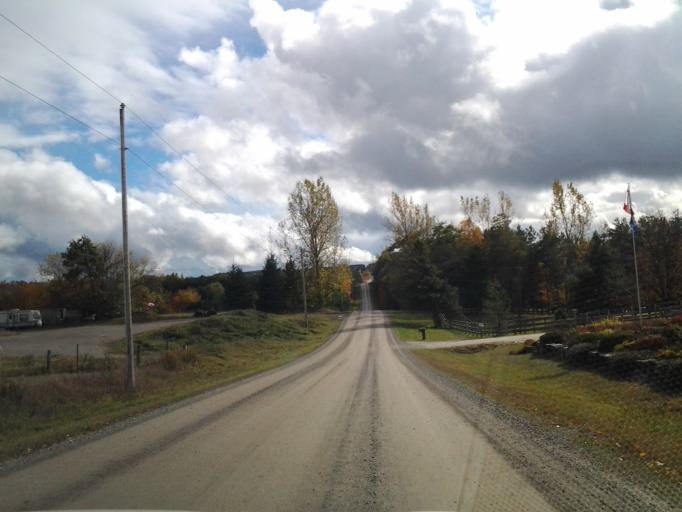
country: CA
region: Ontario
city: Shelburne
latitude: 44.0948
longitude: -80.1063
